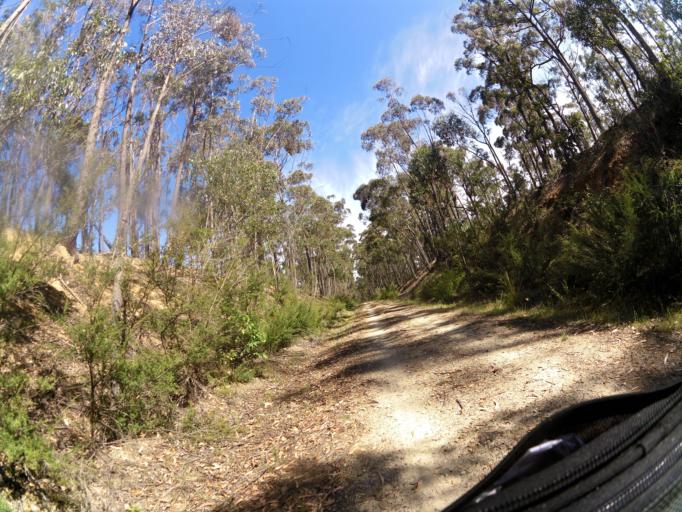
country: AU
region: Victoria
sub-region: East Gippsland
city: Lakes Entrance
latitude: -37.7213
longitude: 148.1459
